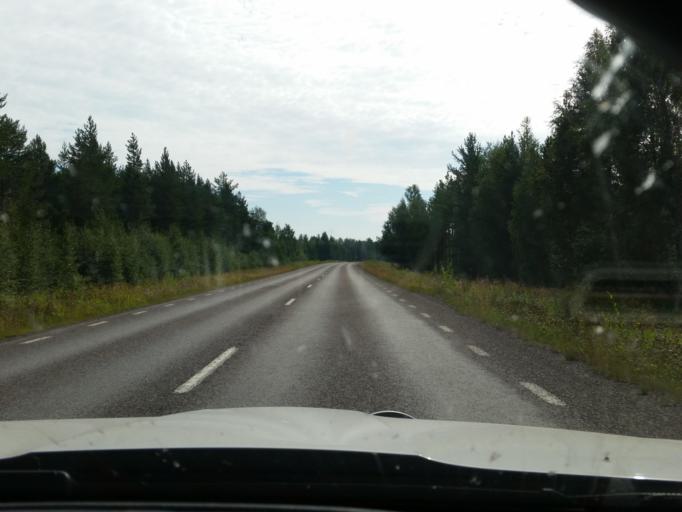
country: SE
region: Norrbotten
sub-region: Alvsbyns Kommun
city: AElvsbyn
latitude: 65.6987
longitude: 20.5769
